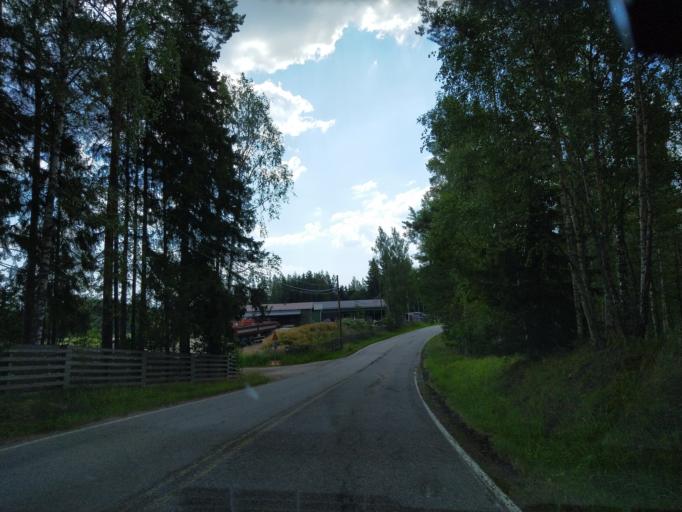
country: FI
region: Uusimaa
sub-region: Helsinki
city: Kirkkonummi
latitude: 60.0610
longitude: 24.4949
